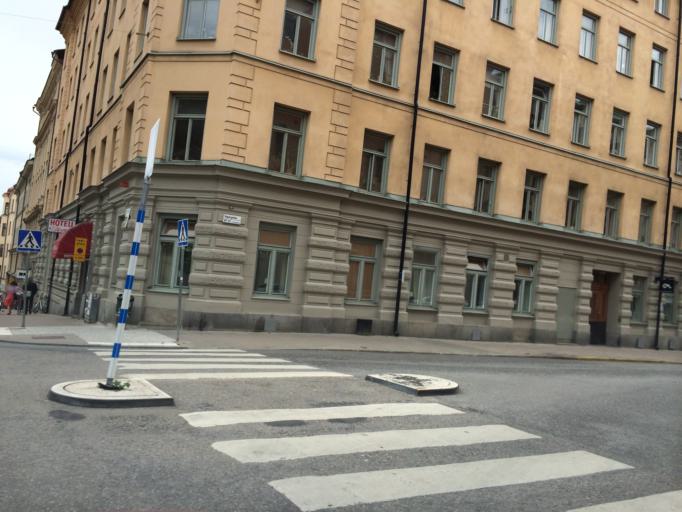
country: SE
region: Stockholm
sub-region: Stockholms Kommun
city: Stockholm
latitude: 59.3379
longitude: 18.0534
